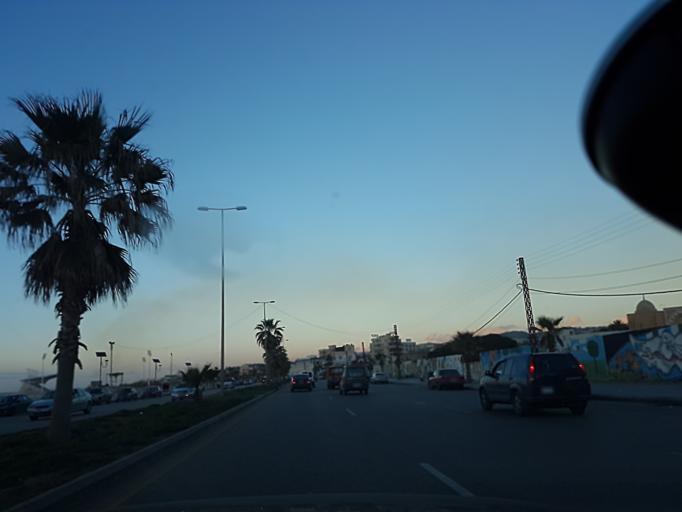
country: LB
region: Liban-Sud
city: Sidon
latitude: 33.5776
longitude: 35.3827
